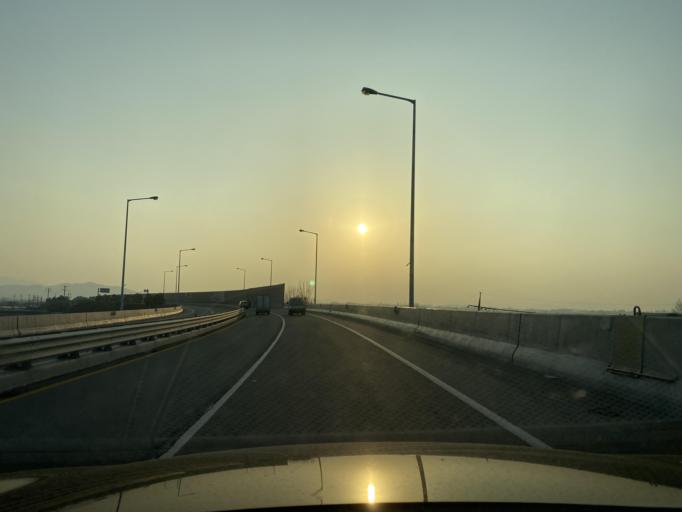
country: KR
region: Chungcheongnam-do
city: Yesan
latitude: 36.7036
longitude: 126.8228
